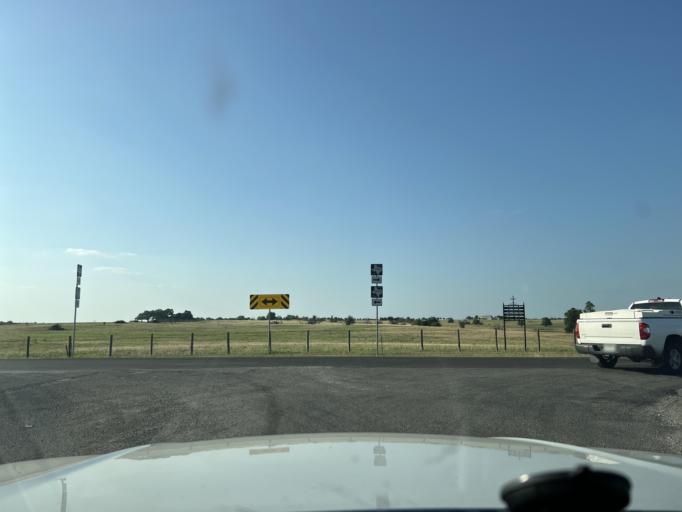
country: US
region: Texas
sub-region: Washington County
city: Brenham
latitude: 30.2405
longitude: -96.2422
